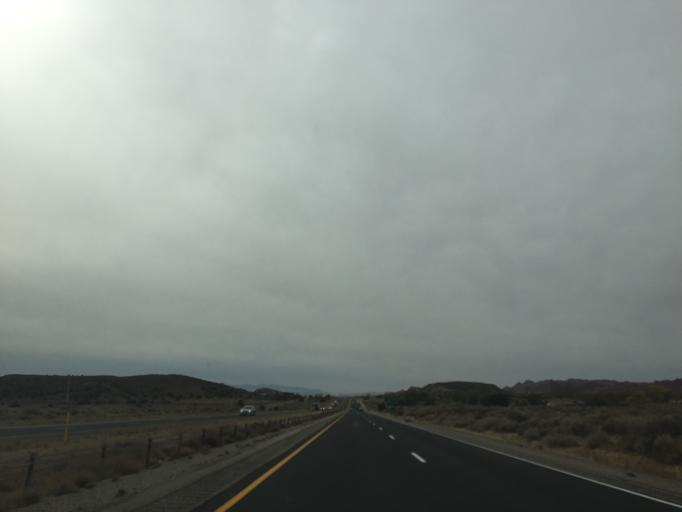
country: US
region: Utah
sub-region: Washington County
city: Toquerville
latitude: 37.2531
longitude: -113.3395
